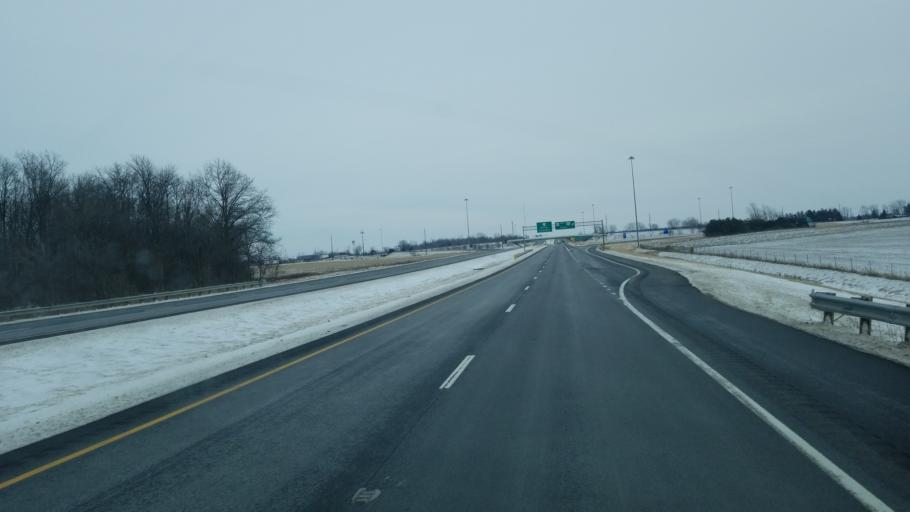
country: US
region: Ohio
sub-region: Wyandot County
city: Carey
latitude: 40.9435
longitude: -83.4075
